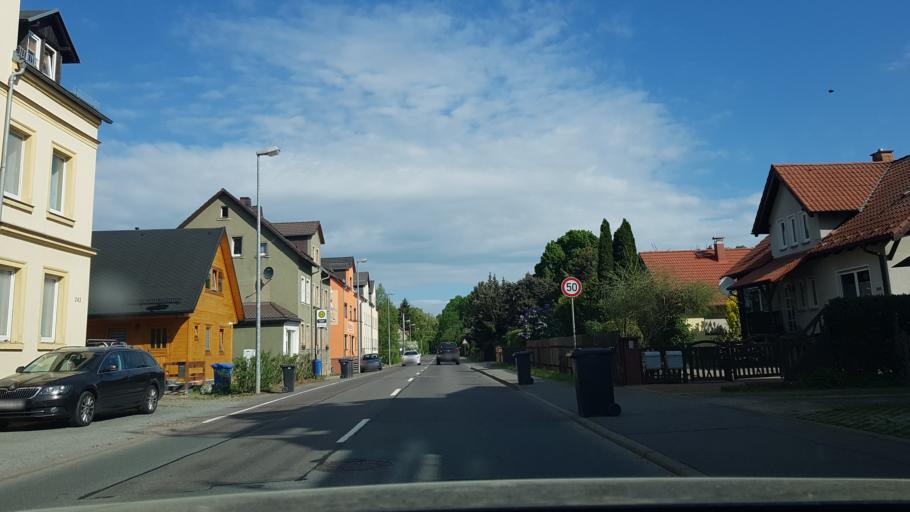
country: DE
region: Saxony
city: Wittgensdorf
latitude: 50.8836
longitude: 12.8973
